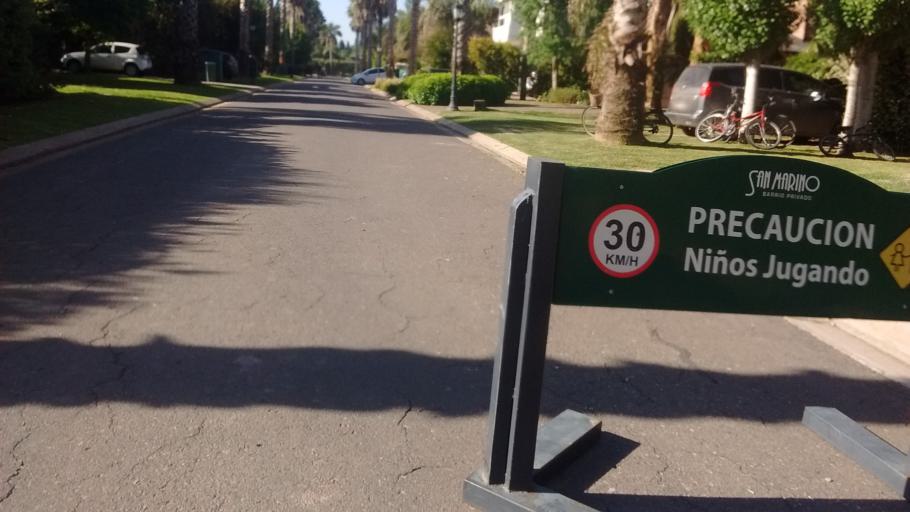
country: AR
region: Santa Fe
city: Funes
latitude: -32.9257
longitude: -60.8212
